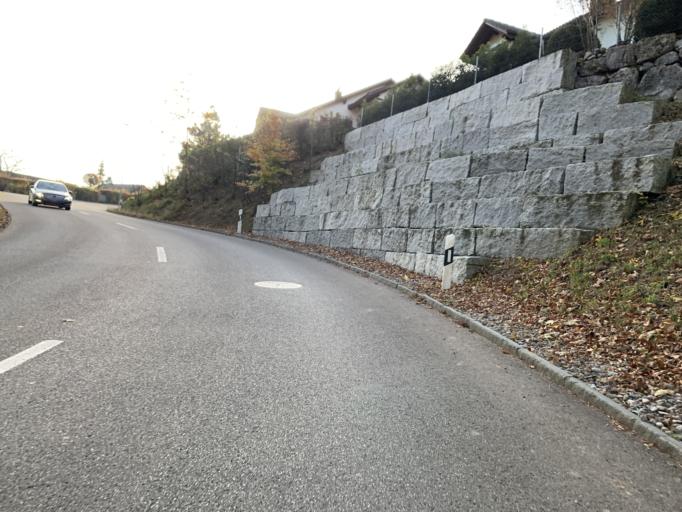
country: CH
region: Zurich
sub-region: Bezirk Hinwil
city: Wald
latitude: 47.2826
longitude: 8.9119
